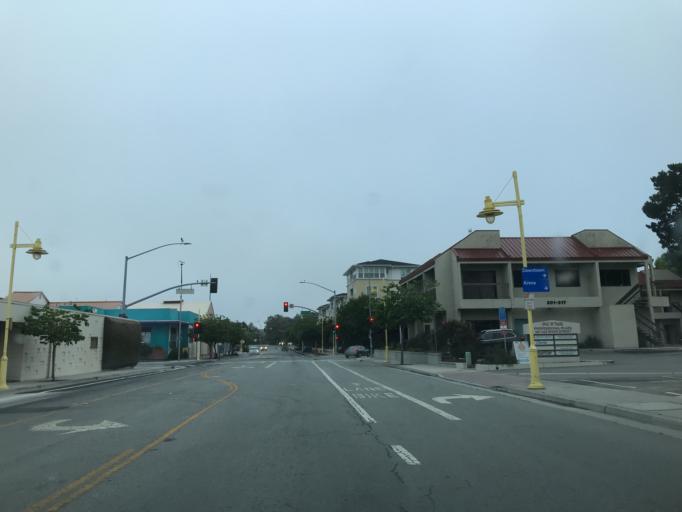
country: US
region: California
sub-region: Santa Cruz County
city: Santa Cruz
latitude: 36.9793
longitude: -122.0277
